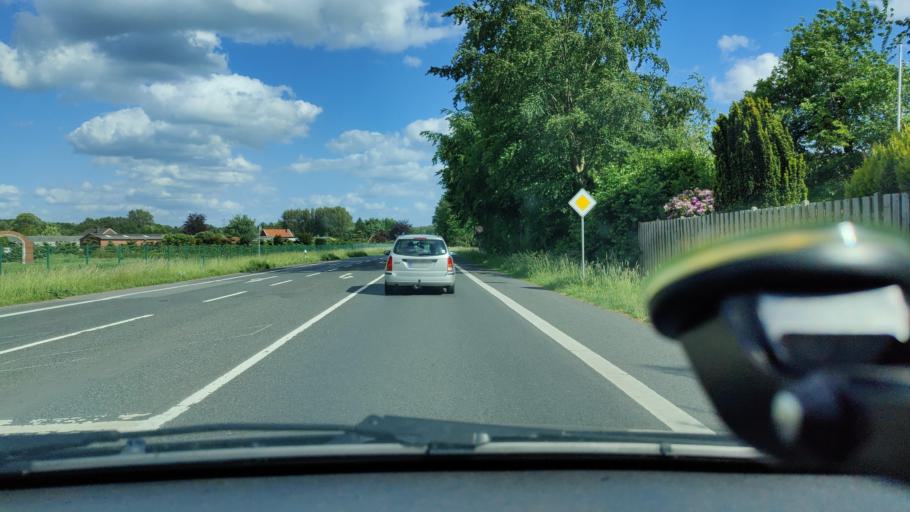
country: DE
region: North Rhine-Westphalia
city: Stadtlohn
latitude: 51.9834
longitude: 6.9488
